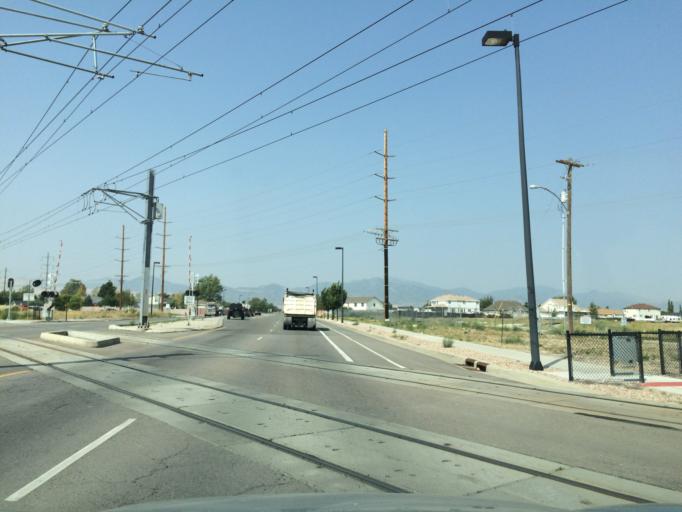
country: US
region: Utah
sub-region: Salt Lake County
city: South Jordan Heights
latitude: 40.5880
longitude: -111.9908
